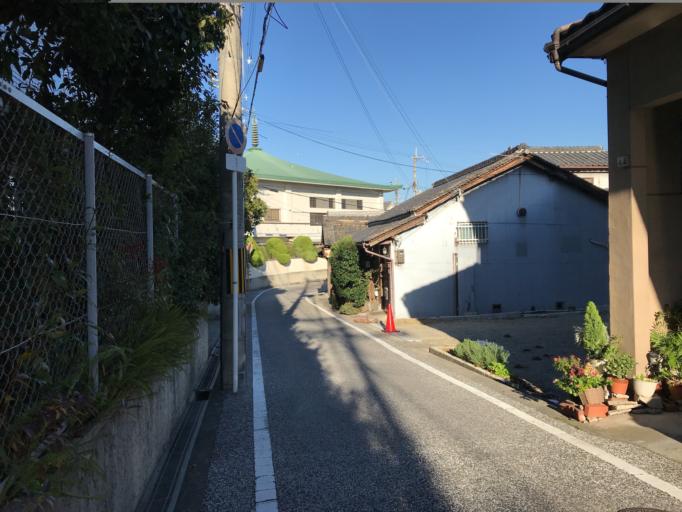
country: JP
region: Osaka
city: Tondabayashicho
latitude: 34.4986
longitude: 135.6001
